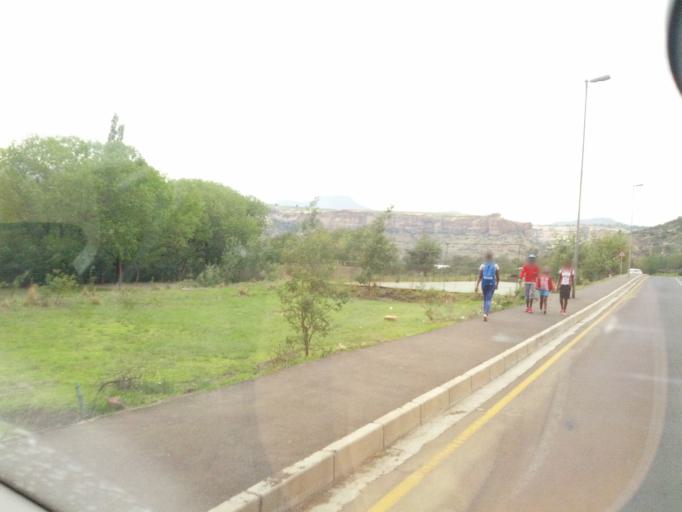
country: LS
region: Maseru
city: Nako
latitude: -29.4634
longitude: 27.7277
